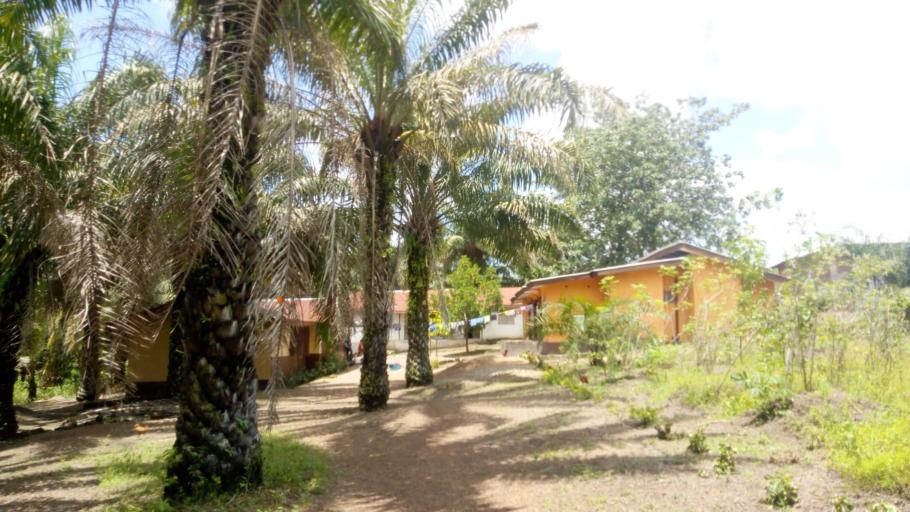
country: SL
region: Northern Province
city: Magburaka
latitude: 8.7128
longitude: -11.9529
